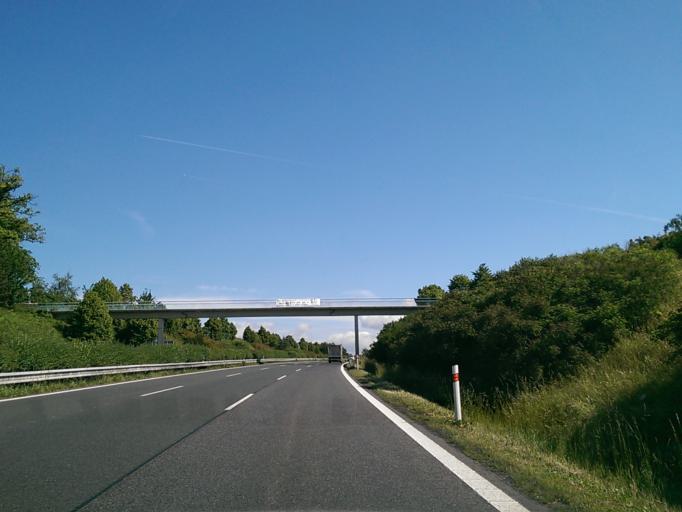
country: CZ
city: Ohrazenice
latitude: 50.6259
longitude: 15.1084
